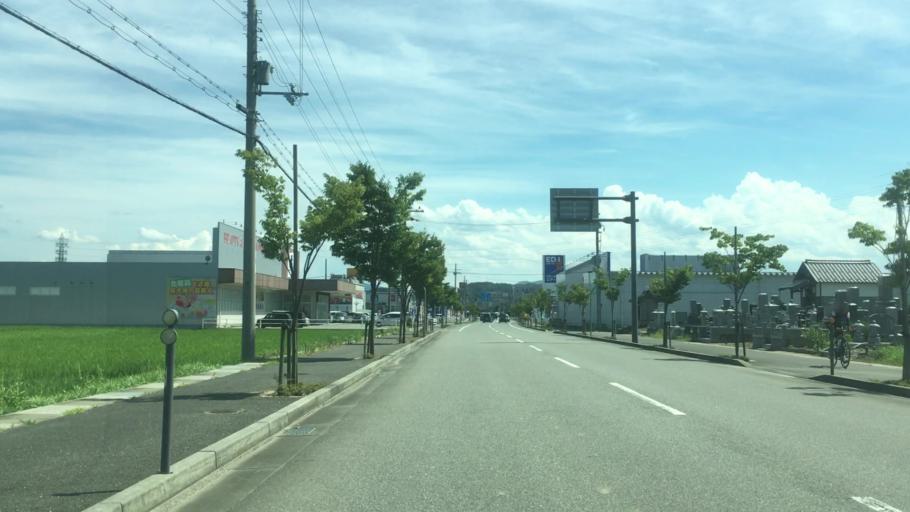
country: JP
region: Hyogo
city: Toyooka
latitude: 35.5570
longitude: 134.8156
